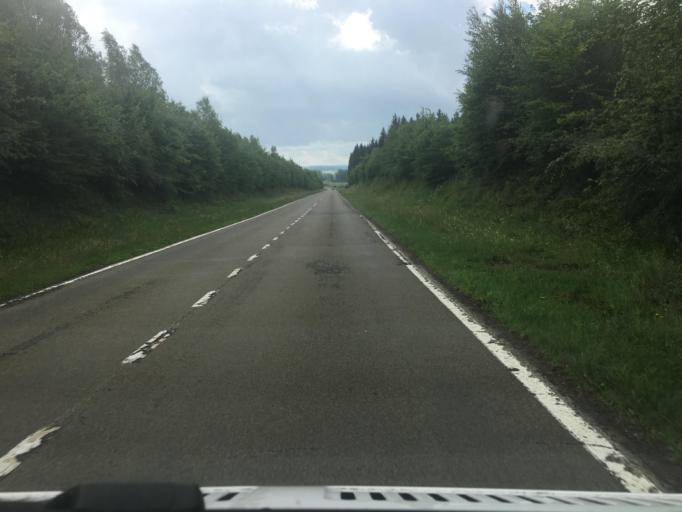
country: BE
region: Wallonia
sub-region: Province du Luxembourg
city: Florenville
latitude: 49.6636
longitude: 5.3309
